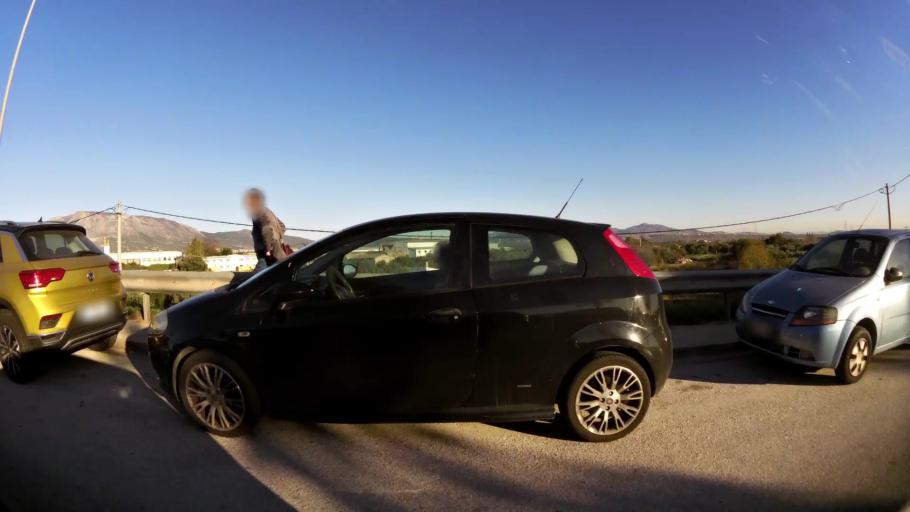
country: GR
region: Attica
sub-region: Nomarchia Anatolikis Attikis
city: Koropi
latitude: 37.9138
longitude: 23.8975
